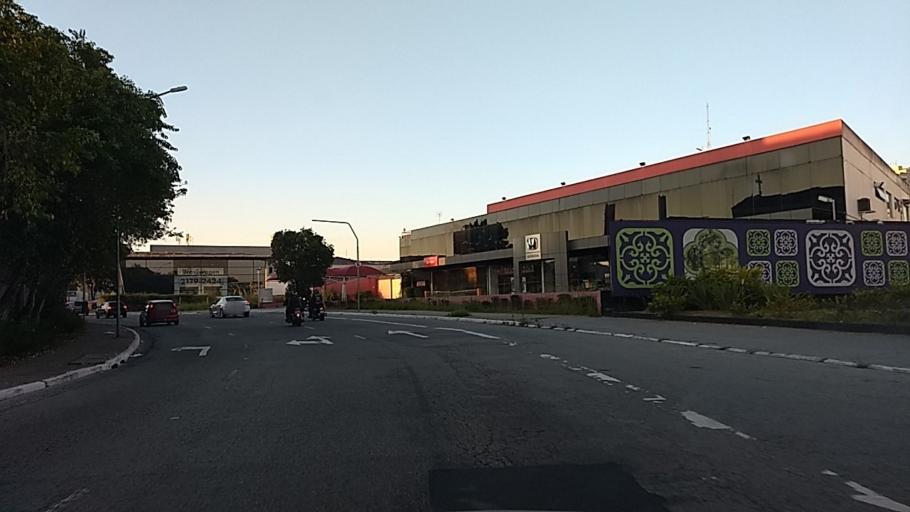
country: BR
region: Sao Paulo
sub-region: Sao Paulo
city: Sao Paulo
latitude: -23.5171
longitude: -46.6086
